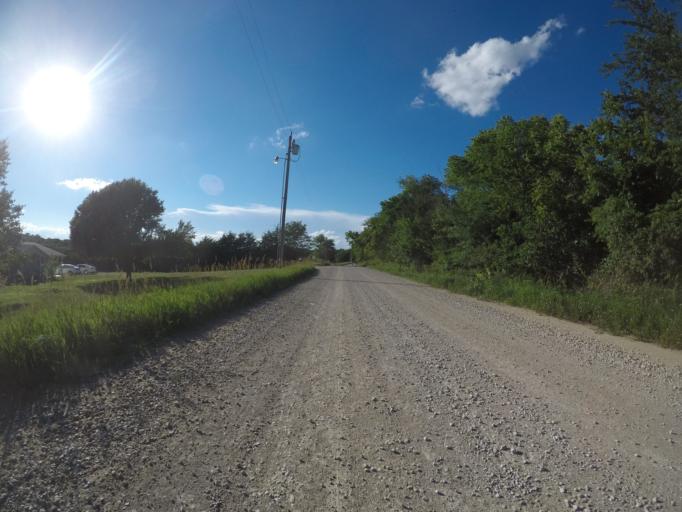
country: US
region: Kansas
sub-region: Riley County
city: Ogden
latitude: 39.2360
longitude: -96.7268
